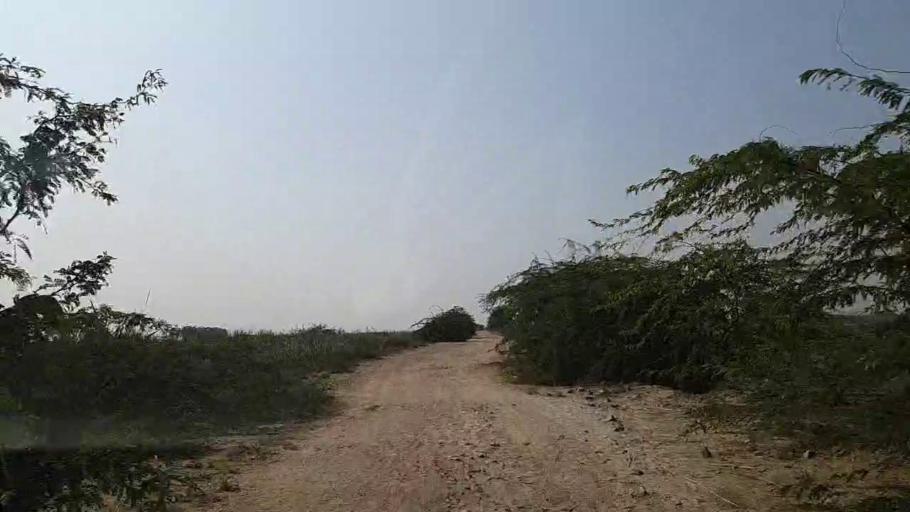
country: PK
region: Sindh
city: Gharo
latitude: 24.6839
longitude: 67.7442
